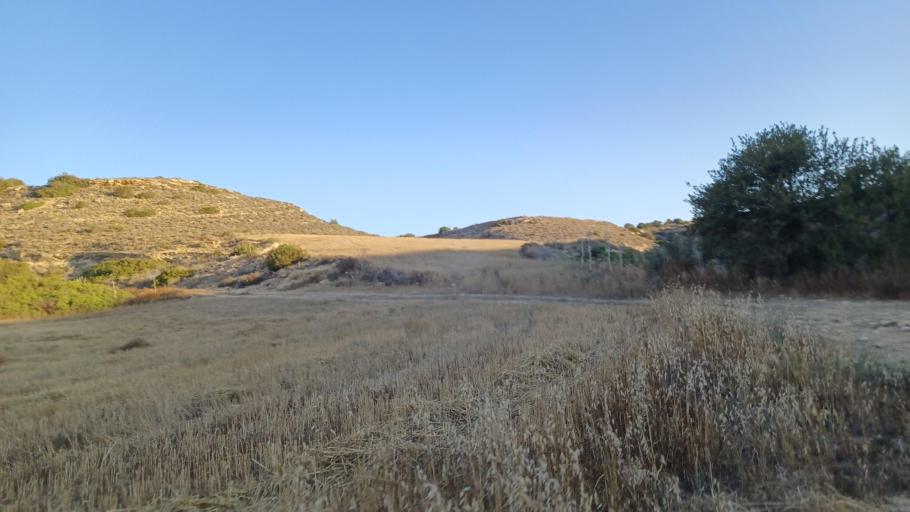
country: CY
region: Larnaka
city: Pyla
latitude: 34.9900
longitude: 33.7109
